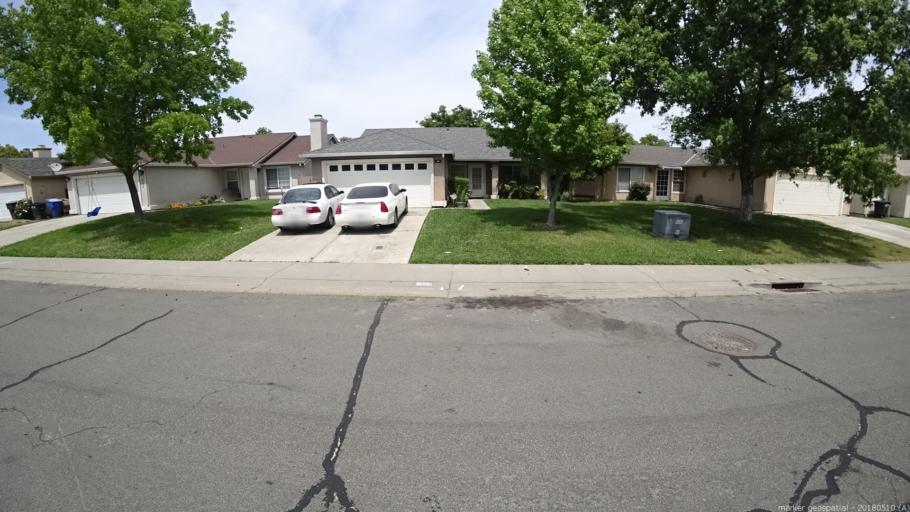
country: US
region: California
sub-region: Sacramento County
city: Rio Linda
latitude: 38.6562
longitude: -121.4642
